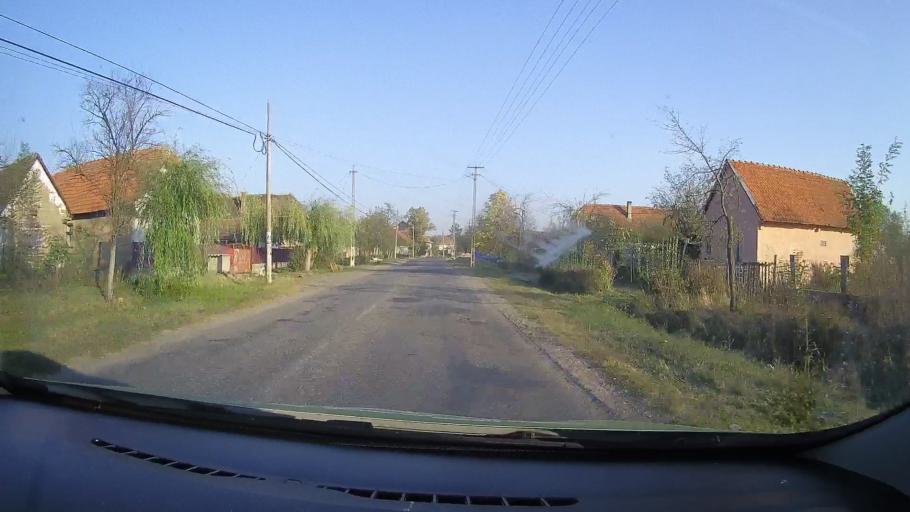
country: RO
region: Arad
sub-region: Comuna Silindia
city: Silindia
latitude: 46.3378
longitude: 21.9227
